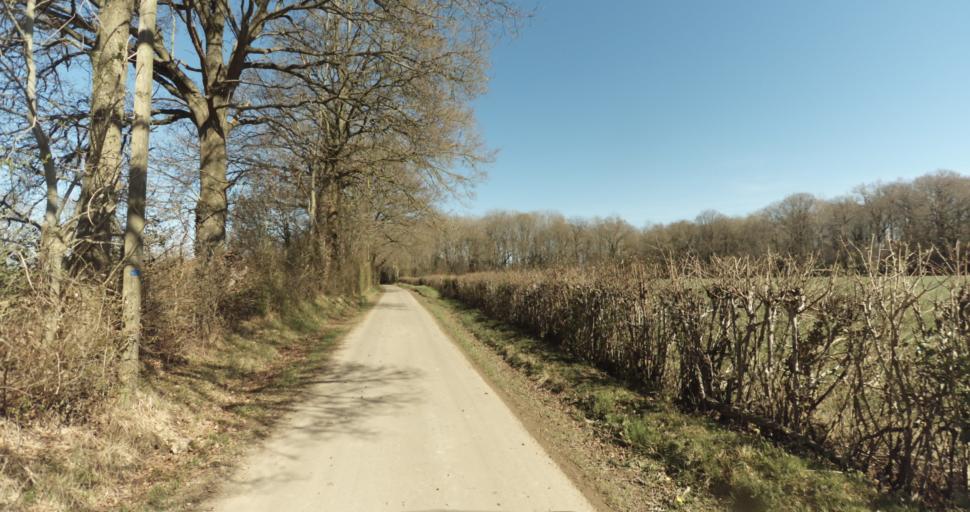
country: FR
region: Lower Normandy
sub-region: Departement du Calvados
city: Livarot
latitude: 48.9839
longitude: 0.0861
